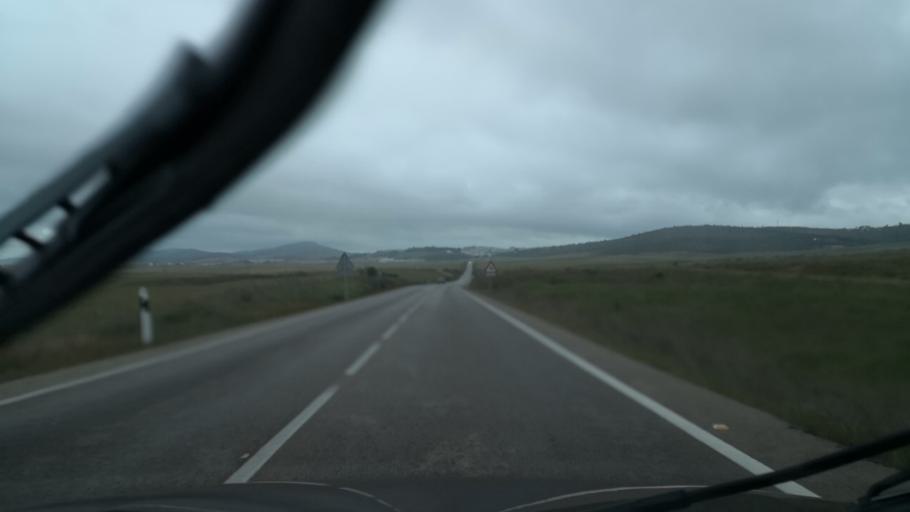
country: ES
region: Extremadura
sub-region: Provincia de Caceres
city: Caceres
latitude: 39.5117
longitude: -6.3943
